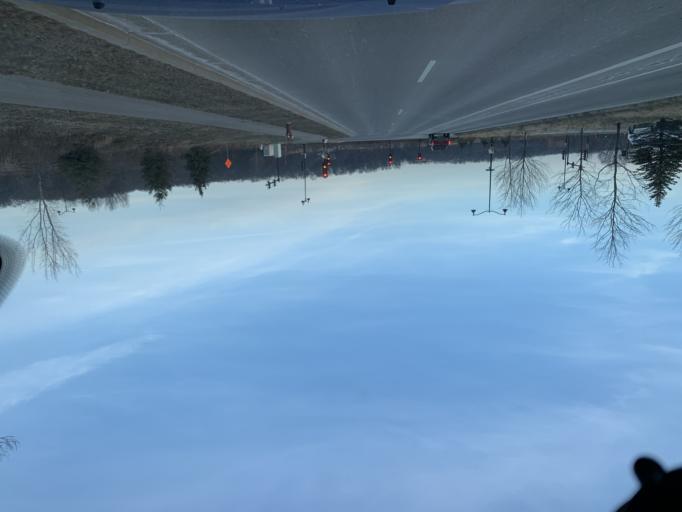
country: US
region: Wisconsin
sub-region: Dane County
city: Verona
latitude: 43.0124
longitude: -89.5581
